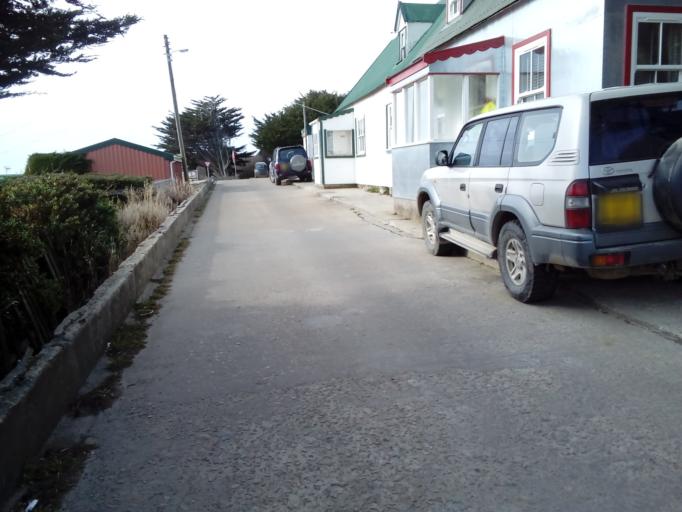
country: FK
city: Stanley
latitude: -51.6934
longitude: -57.8643
